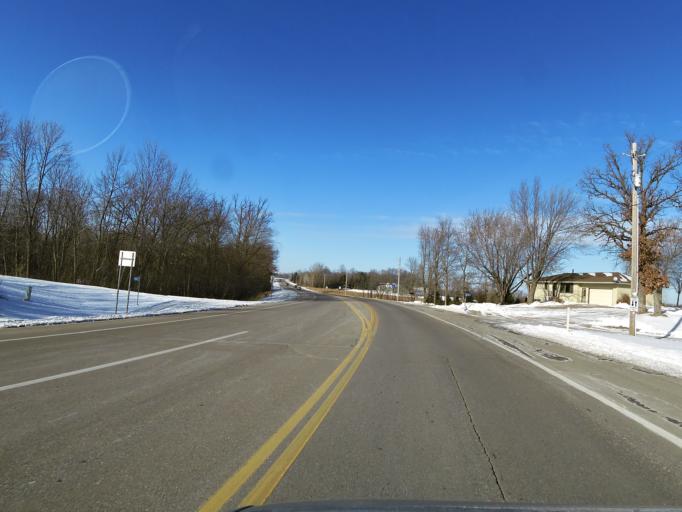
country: US
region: Minnesota
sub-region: Scott County
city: Prior Lake
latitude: 44.7279
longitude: -93.4906
